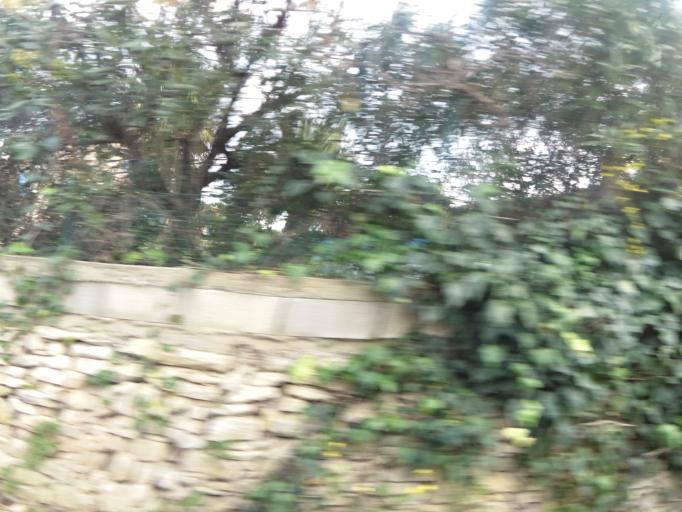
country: FR
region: Languedoc-Roussillon
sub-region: Departement du Gard
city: Clarensac
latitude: 43.8312
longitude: 4.2012
